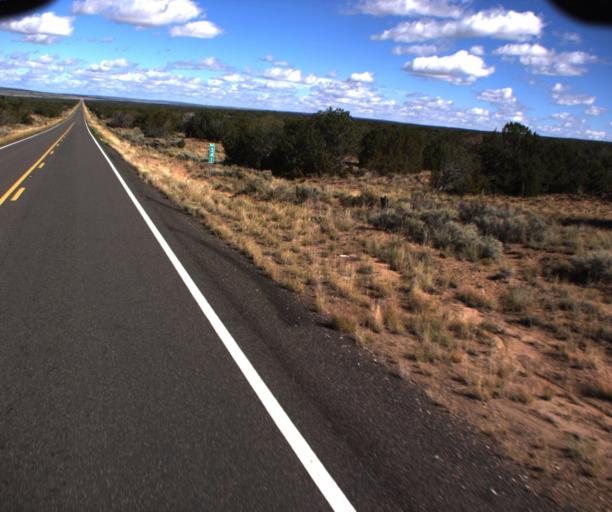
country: US
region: Arizona
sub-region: Apache County
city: Saint Johns
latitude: 34.8502
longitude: -109.2376
